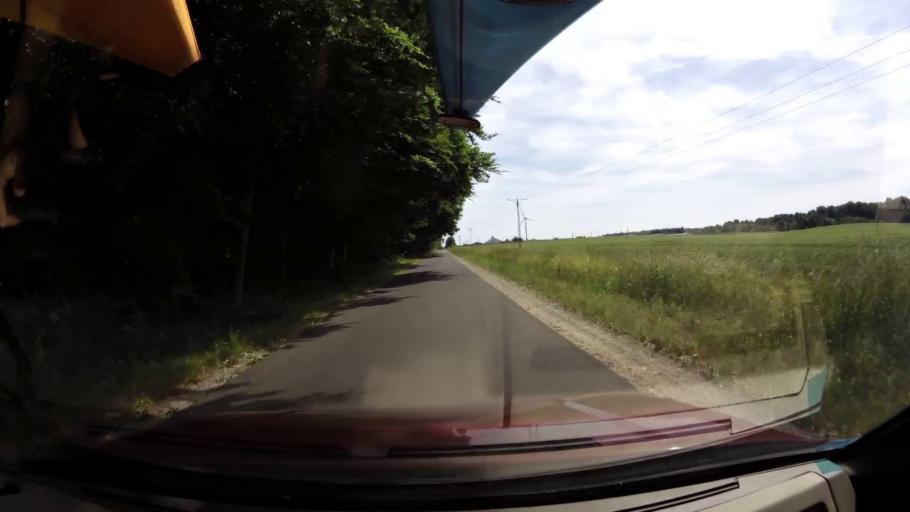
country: PL
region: West Pomeranian Voivodeship
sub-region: Powiat slawienski
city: Darlowo
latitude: 54.3129
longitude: 16.4468
